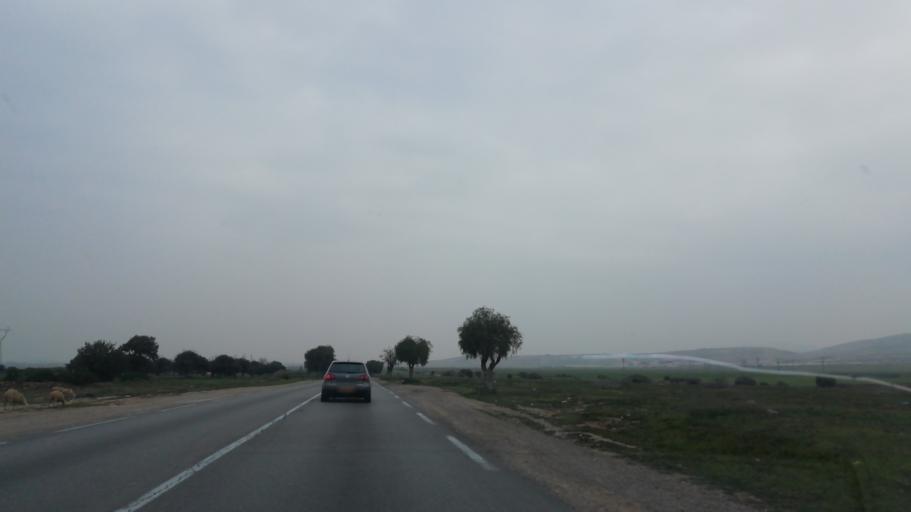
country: DZ
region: Mascara
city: Sig
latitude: 35.5464
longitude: -0.2992
